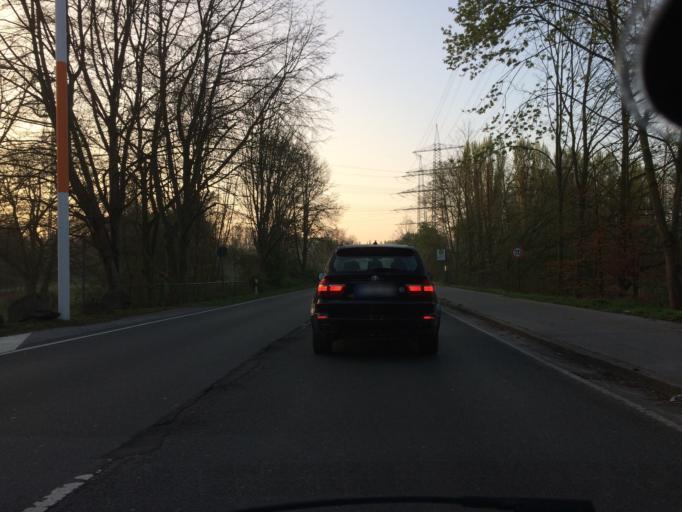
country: DE
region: North Rhine-Westphalia
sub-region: Regierungsbezirk Munster
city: Gelsenkirchen
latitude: 51.4811
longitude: 7.1019
